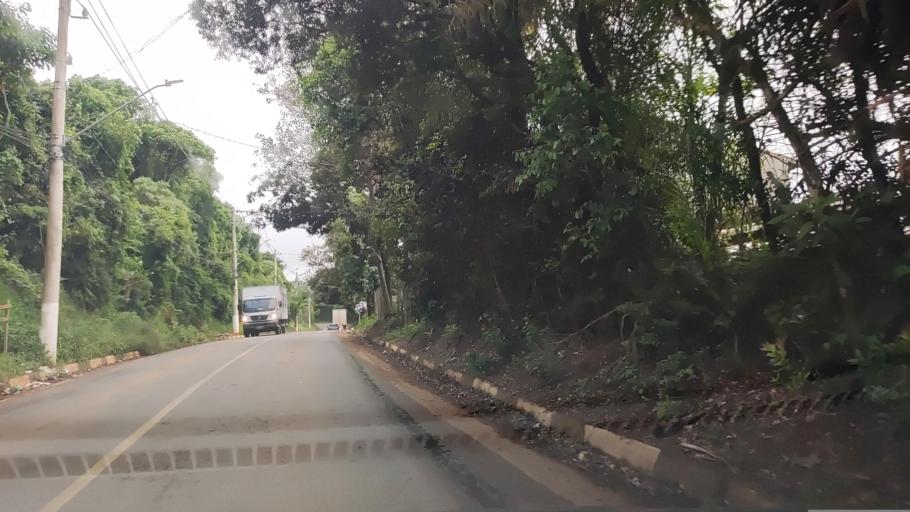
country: BR
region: Sao Paulo
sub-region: Vargem Grande Paulista
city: Vargem Grande Paulista
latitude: -23.6545
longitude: -47.0489
